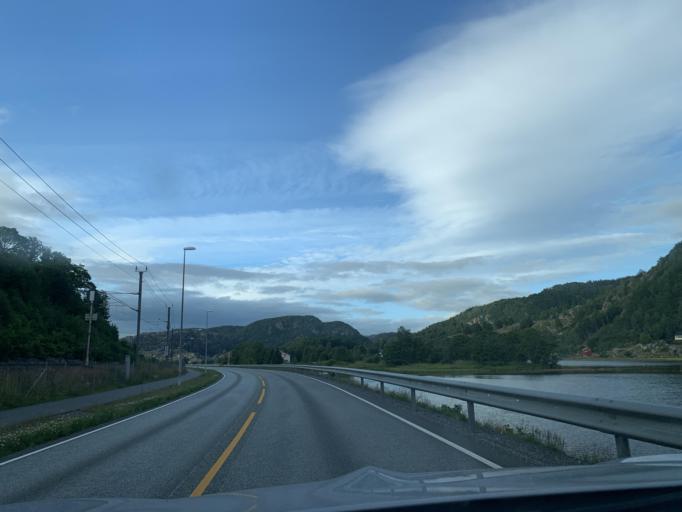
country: NO
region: Rogaland
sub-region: Eigersund
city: Egersund
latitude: 58.4641
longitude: 6.0222
